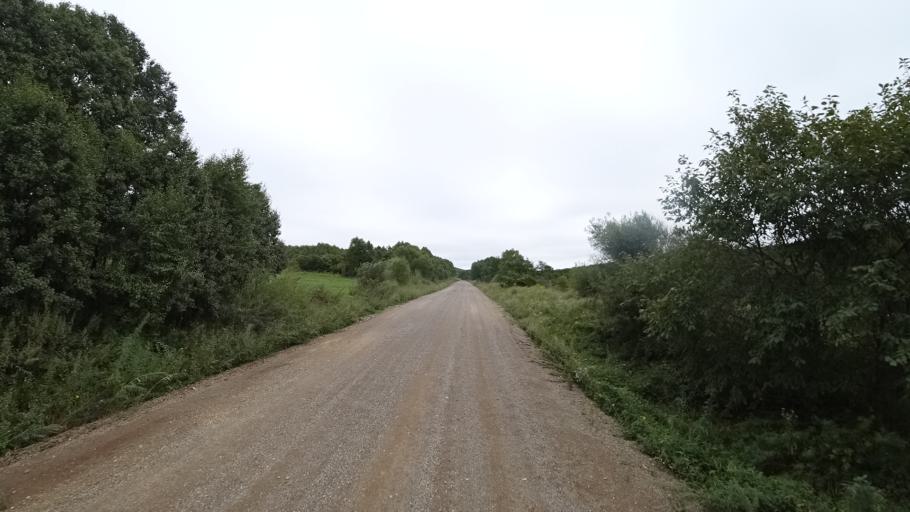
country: RU
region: Primorskiy
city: Ivanovka
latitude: 44.0555
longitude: 132.4803
